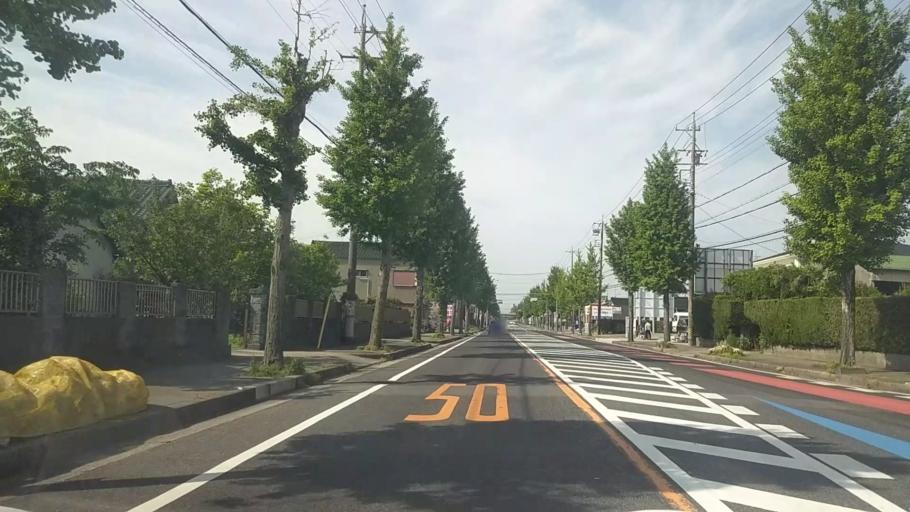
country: JP
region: Aichi
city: Okazaki
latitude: 34.9456
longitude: 137.1549
